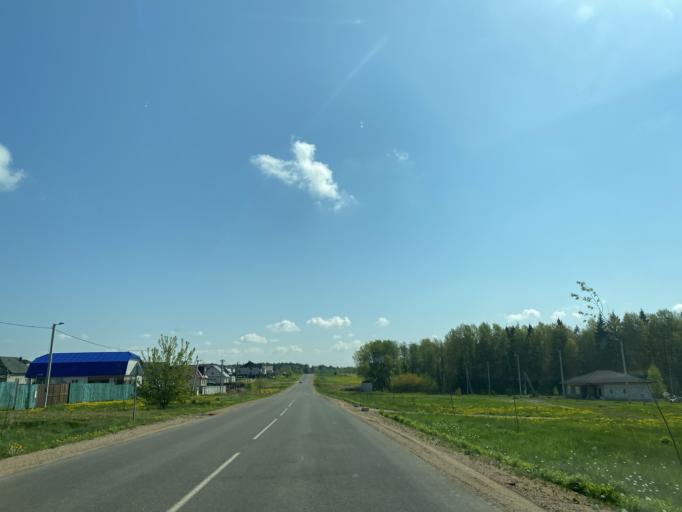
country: BY
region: Minsk
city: Horad Barysaw
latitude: 54.1788
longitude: 28.5562
